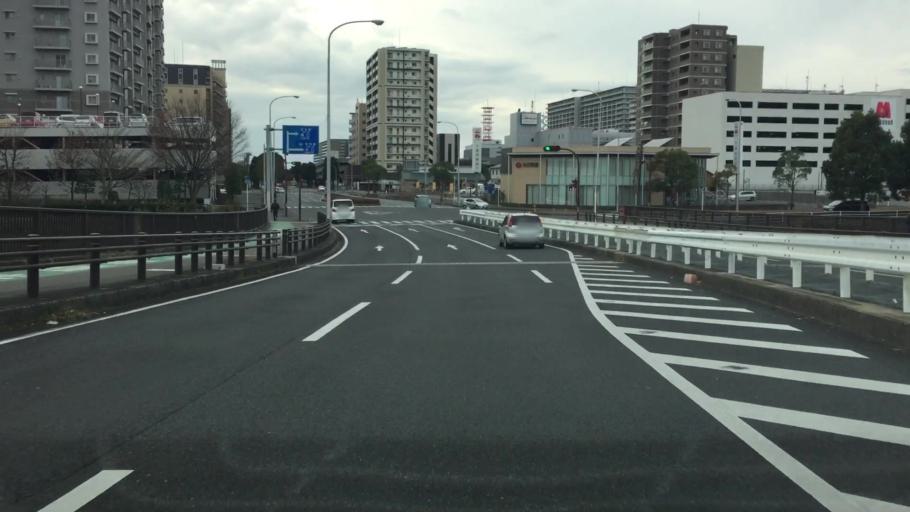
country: JP
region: Chiba
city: Shiroi
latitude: 35.7985
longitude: 140.1208
